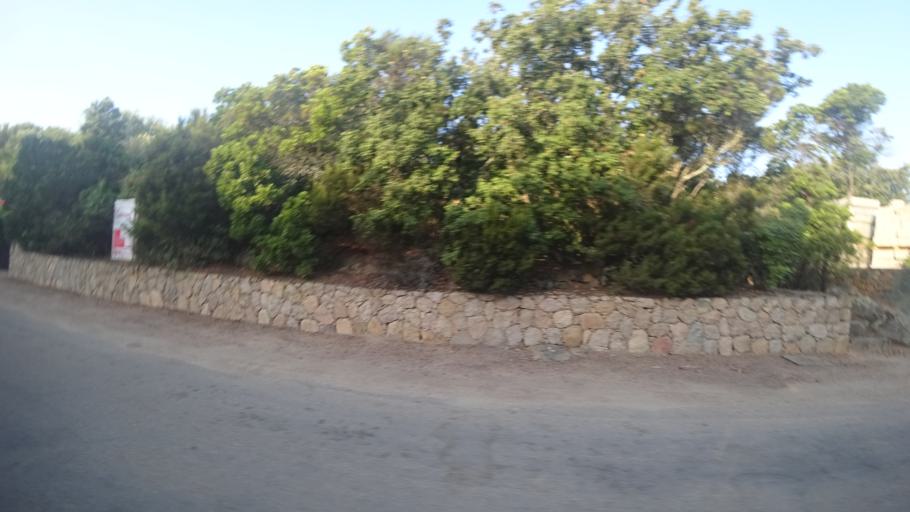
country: FR
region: Corsica
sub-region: Departement de la Corse-du-Sud
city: Porto-Vecchio
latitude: 41.6202
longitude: 9.3538
